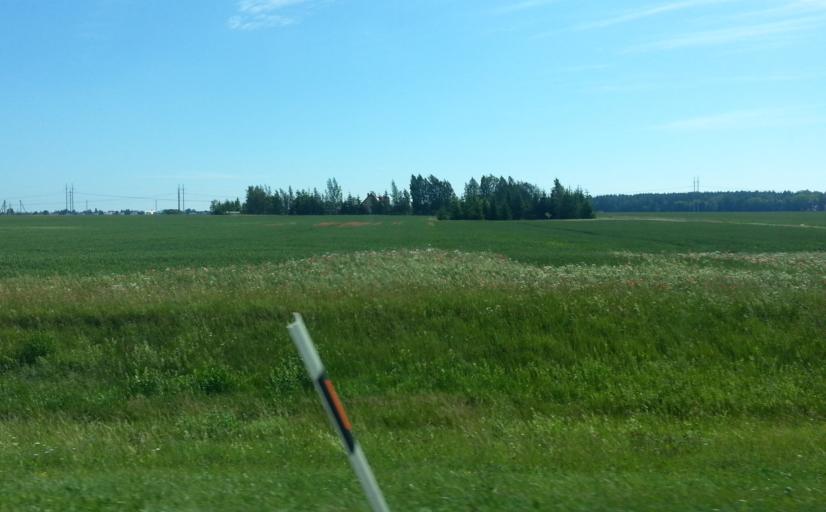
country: LT
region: Panevezys
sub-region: Panevezys City
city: Panevezys
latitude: 55.6993
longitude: 24.2735
